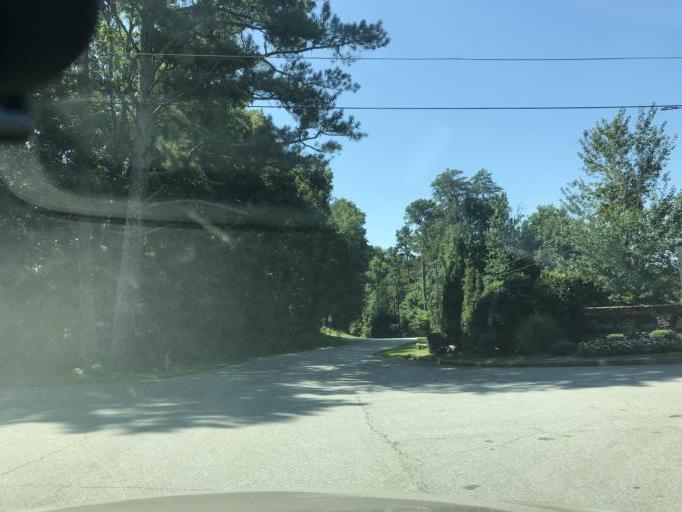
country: US
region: Georgia
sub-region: Forsyth County
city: Cumming
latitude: 34.2019
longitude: -84.1105
